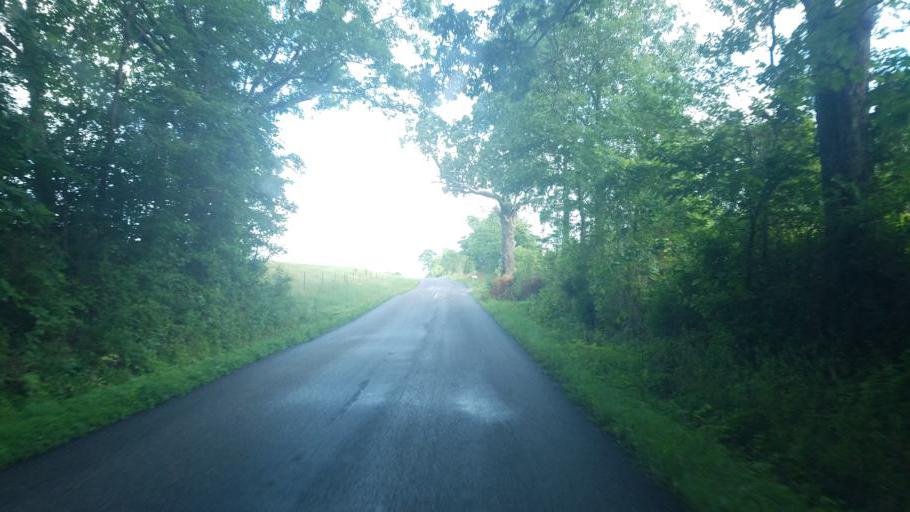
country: US
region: Ohio
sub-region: Gallia County
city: Gallipolis
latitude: 38.7708
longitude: -82.3719
